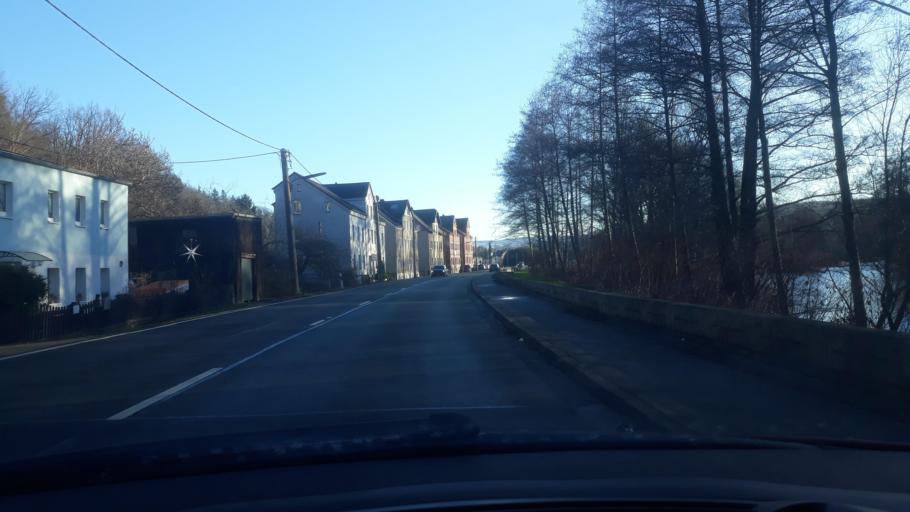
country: DE
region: Saxony
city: Wilkau-Hasslau
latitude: 50.6722
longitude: 12.5327
